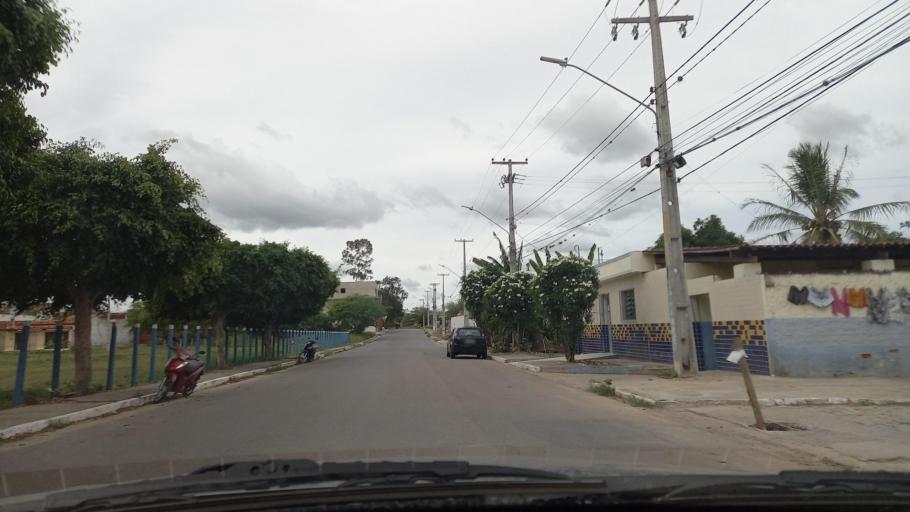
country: BR
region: Pernambuco
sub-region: Gravata
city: Gravata
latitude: -8.2071
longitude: -35.5869
